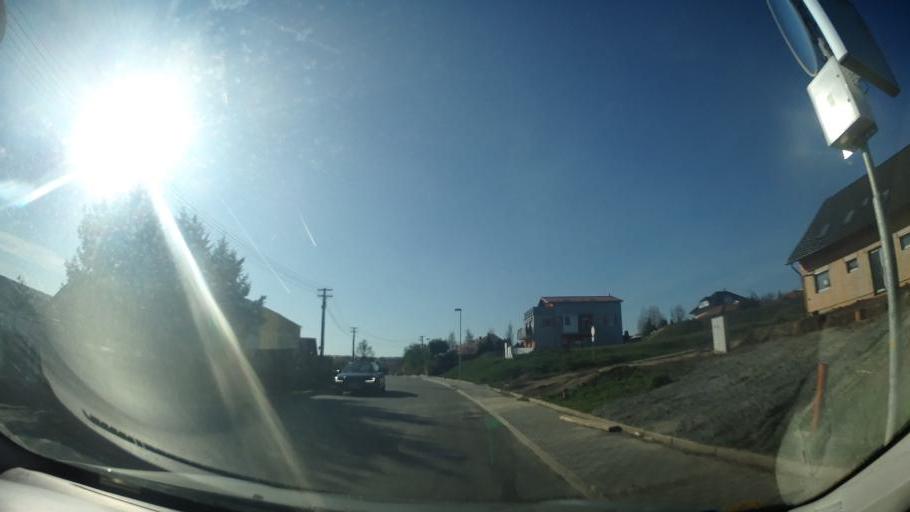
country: CZ
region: South Moravian
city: Moravany
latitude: 49.1465
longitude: 16.5839
